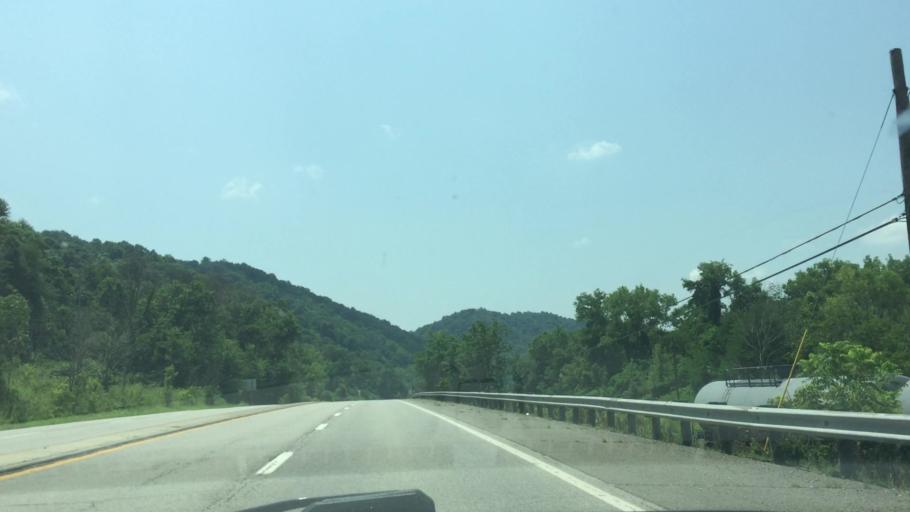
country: US
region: Ohio
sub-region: Belmont County
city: Powhatan Point
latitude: 39.8054
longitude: -80.8173
